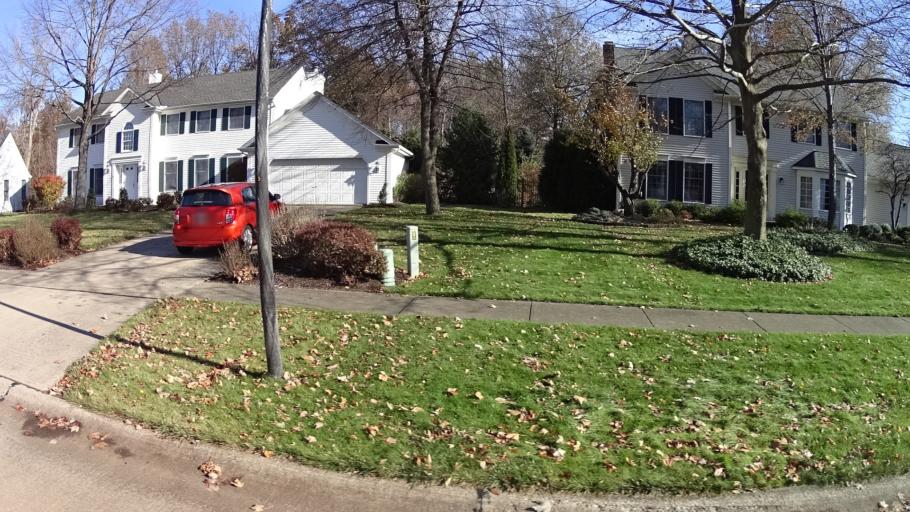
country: US
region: Ohio
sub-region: Lorain County
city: Avon Lake
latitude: 41.4965
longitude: -81.9948
